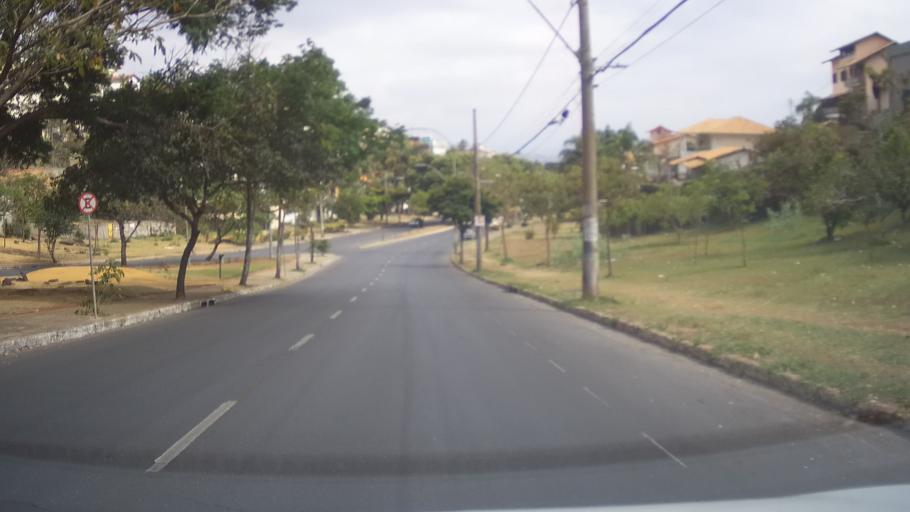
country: BR
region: Minas Gerais
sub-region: Belo Horizonte
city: Belo Horizonte
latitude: -19.9553
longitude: -43.9150
